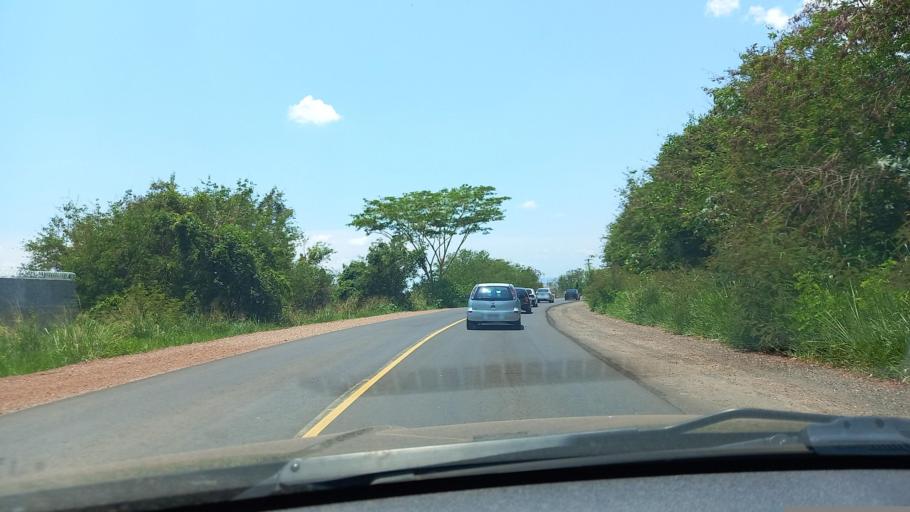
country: BR
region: Sao Paulo
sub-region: Itapira
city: Itapira
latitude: -22.3785
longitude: -46.8689
